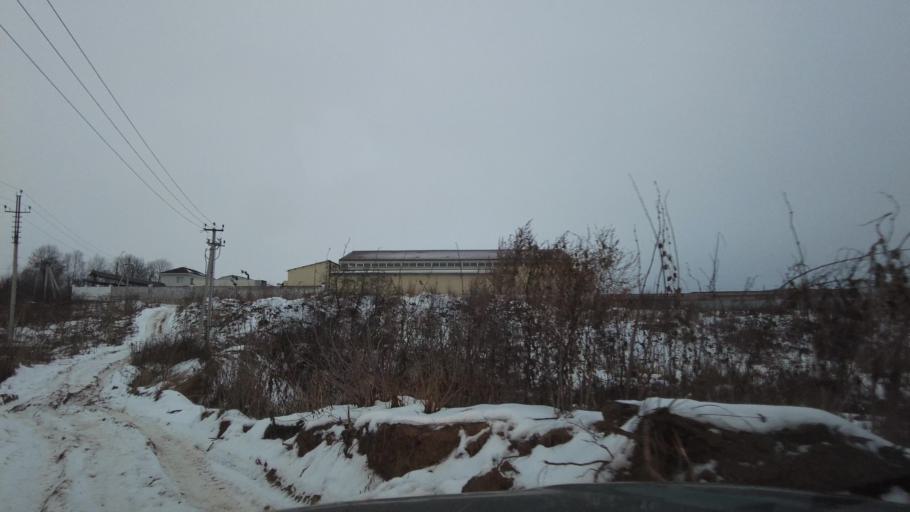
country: RU
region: Moskovskaya
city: Novopodrezkovo
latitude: 55.9899
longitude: 37.3935
